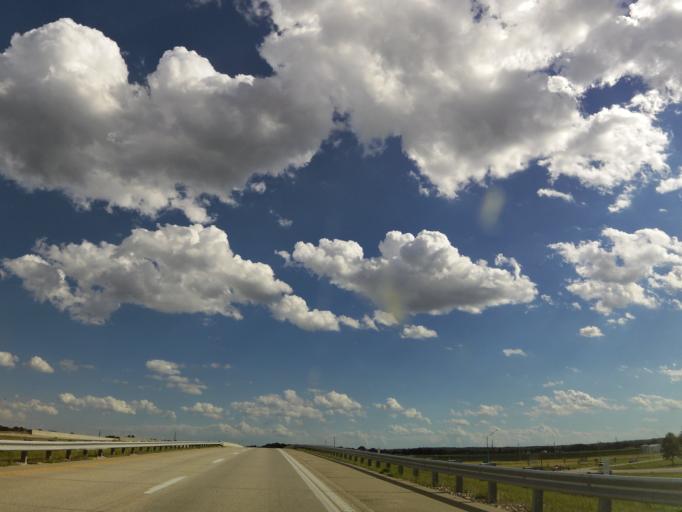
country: US
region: Illinois
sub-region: Hancock County
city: Warsaw
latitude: 40.3955
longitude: -91.5729
